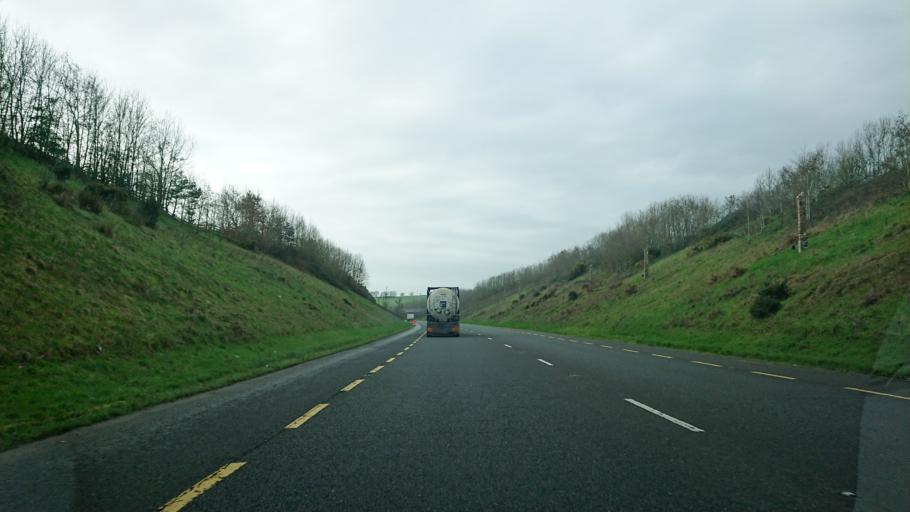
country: IE
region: Munster
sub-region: County Cork
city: Youghal
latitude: 51.9686
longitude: -7.8776
